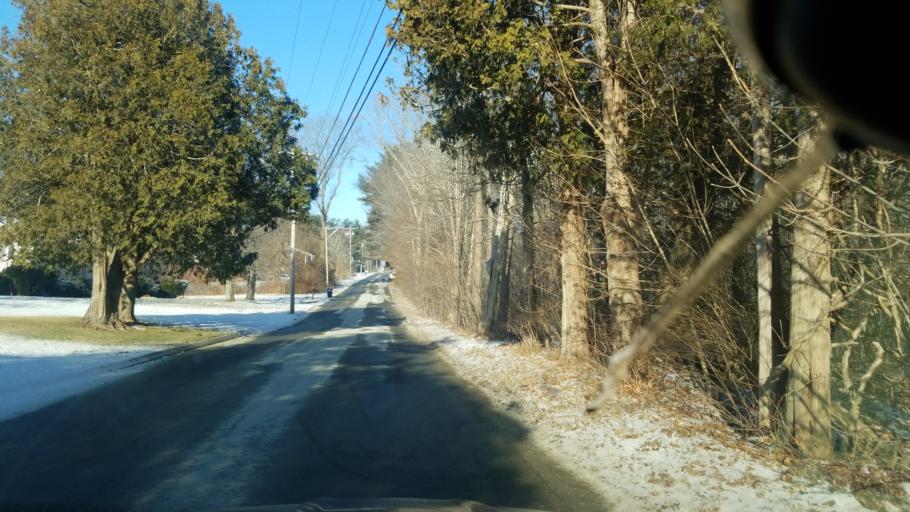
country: US
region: Connecticut
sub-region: Windham County
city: East Brooklyn
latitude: 41.8039
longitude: -71.9020
